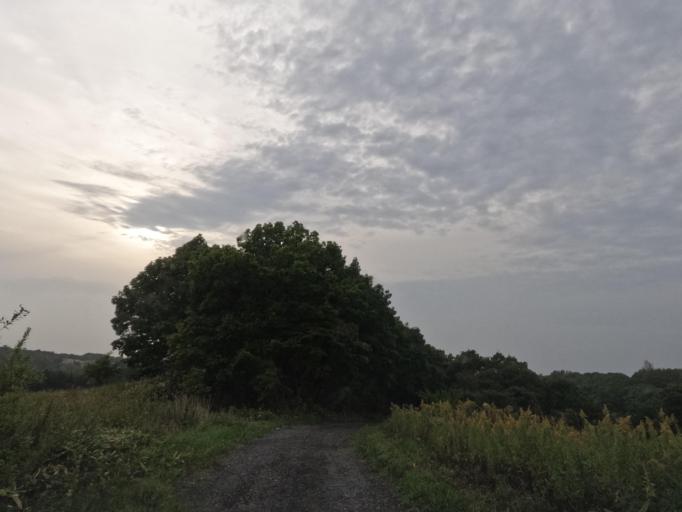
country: JP
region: Hokkaido
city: Date
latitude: 42.4134
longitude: 140.9308
